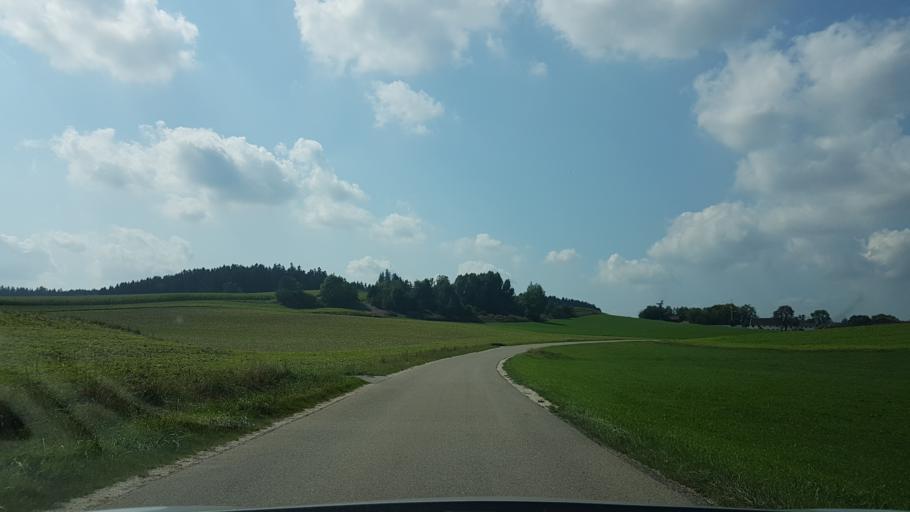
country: DE
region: Bavaria
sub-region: Upper Bavaria
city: Steinkirchen
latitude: 48.3711
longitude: 12.0624
